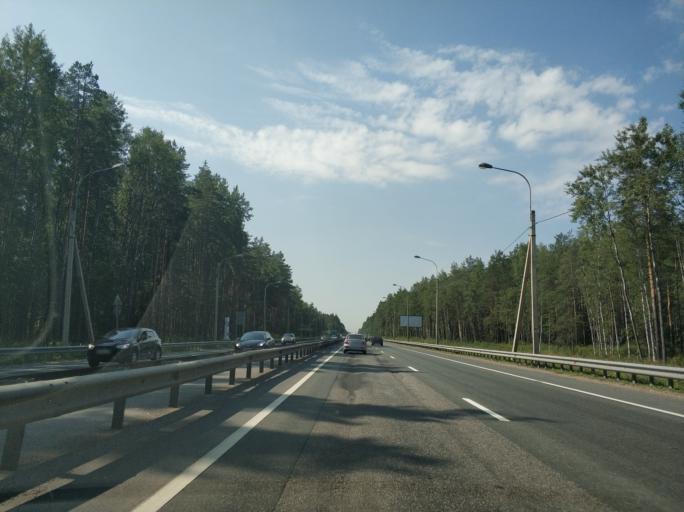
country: RU
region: Leningrad
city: Yanino Vtoroye
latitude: 60.0034
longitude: 30.5605
